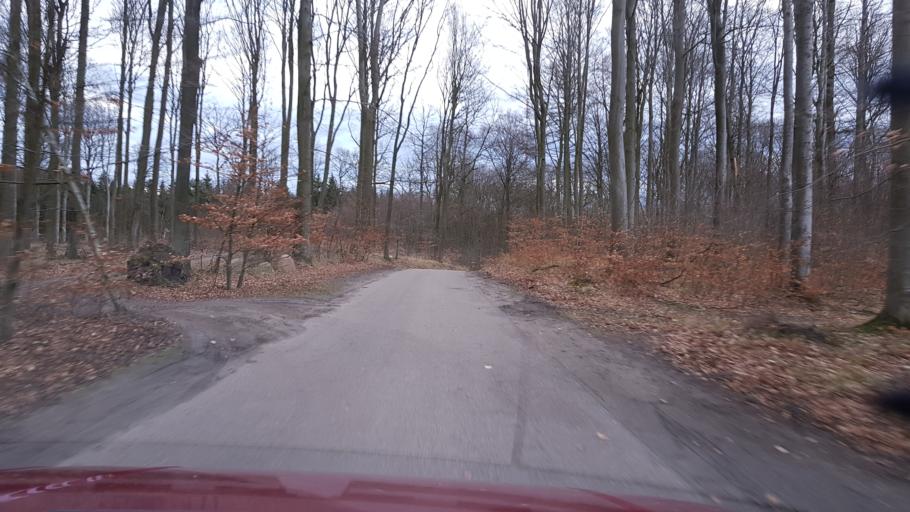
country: PL
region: West Pomeranian Voivodeship
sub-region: Powiat gryfinski
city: Stare Czarnowo
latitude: 53.3354
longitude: 14.6620
